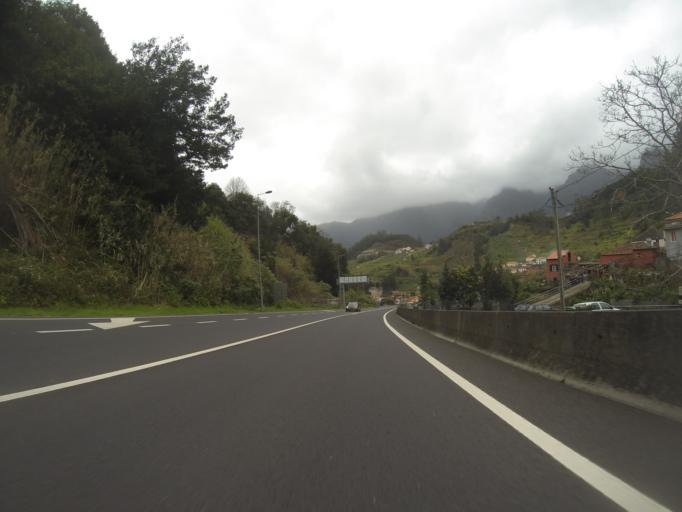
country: PT
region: Madeira
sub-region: Sao Vicente
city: Sao Vicente
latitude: 32.7718
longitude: -17.0306
